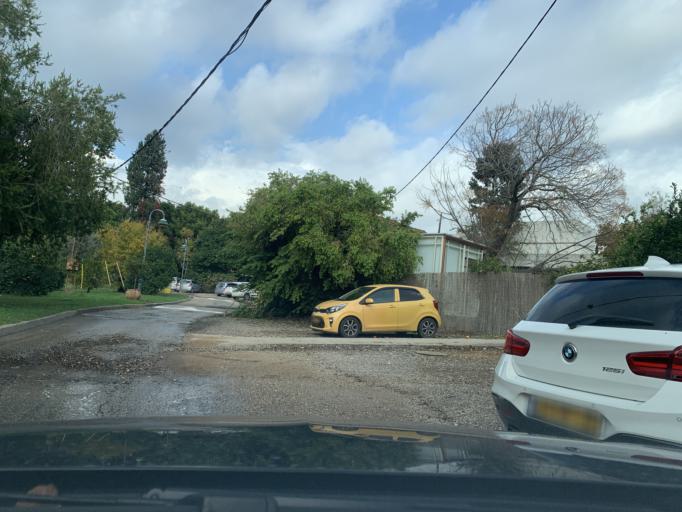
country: PS
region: West Bank
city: Qalqilyah
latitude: 32.1975
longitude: 34.9500
